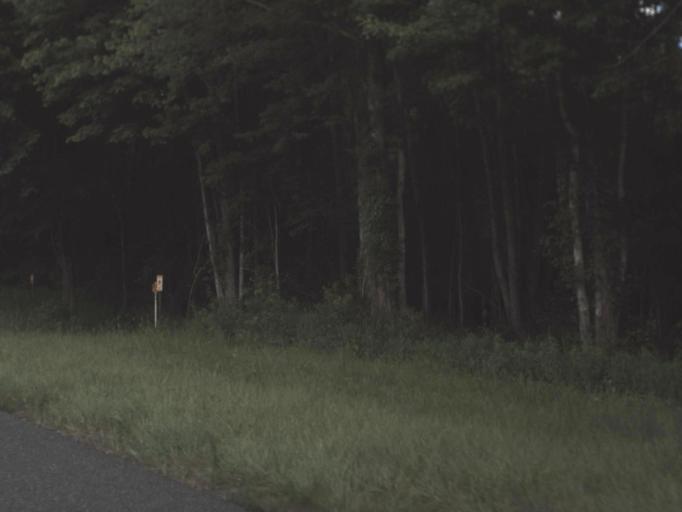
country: US
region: Florida
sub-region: Taylor County
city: Perry
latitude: 30.2257
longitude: -83.6777
